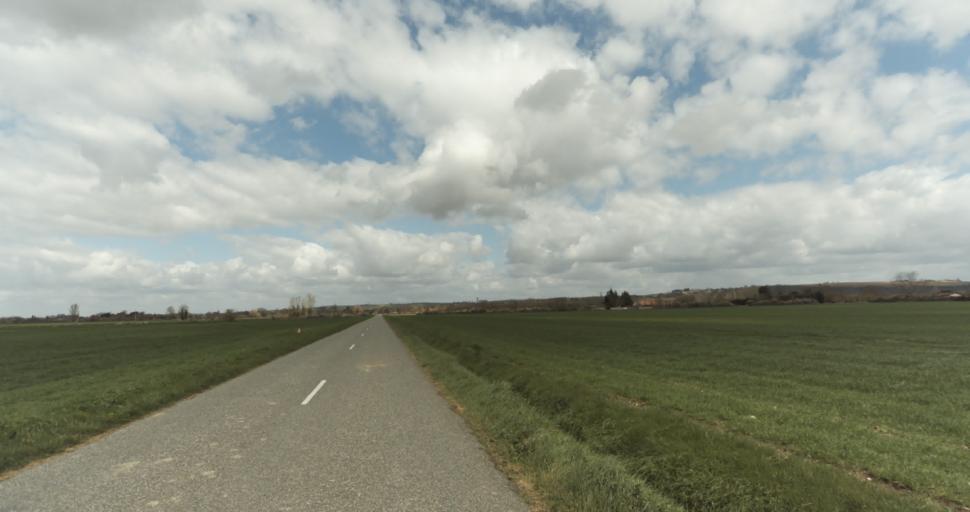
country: FR
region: Midi-Pyrenees
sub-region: Departement de la Haute-Garonne
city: Auterive
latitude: 43.3256
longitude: 1.4768
